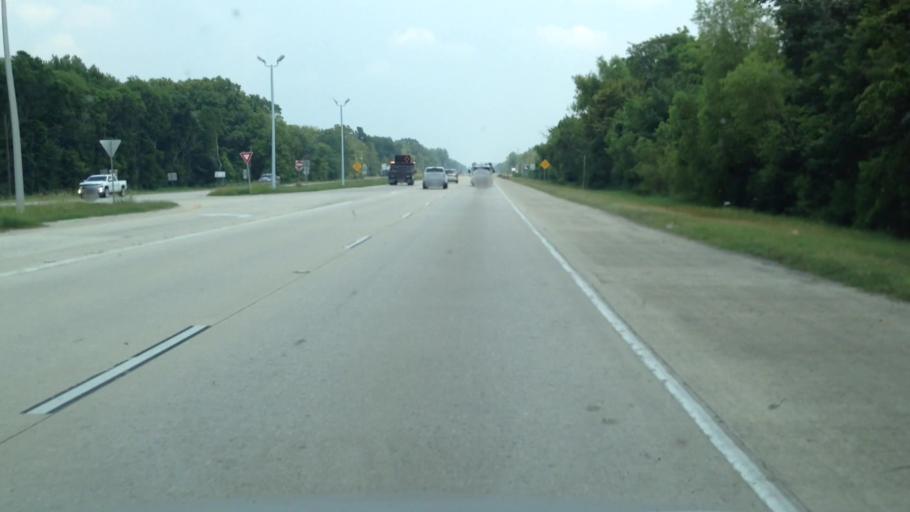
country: US
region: Louisiana
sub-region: West Baton Rouge Parish
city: Erwinville
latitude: 30.5089
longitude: -91.3358
